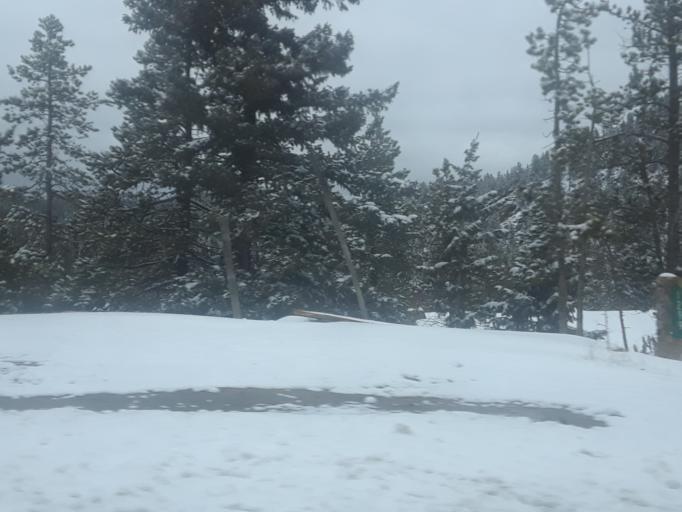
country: US
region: Colorado
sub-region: Boulder County
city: Coal Creek
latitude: 39.9252
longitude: -105.4131
